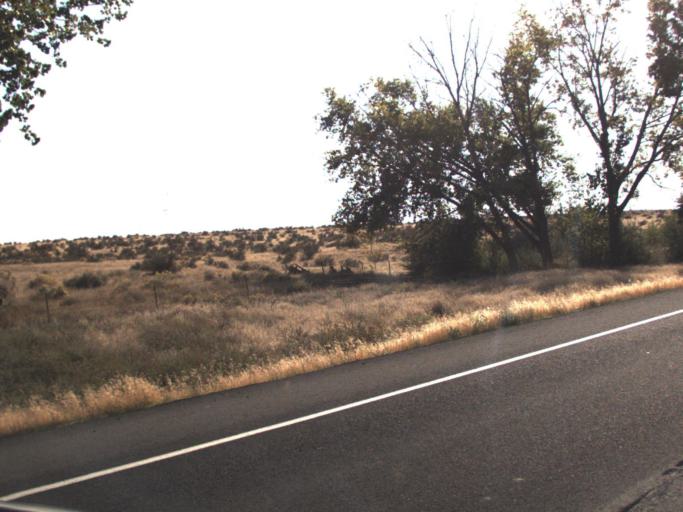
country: US
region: Oregon
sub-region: Morrow County
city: Irrigon
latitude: 45.9485
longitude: -119.4397
